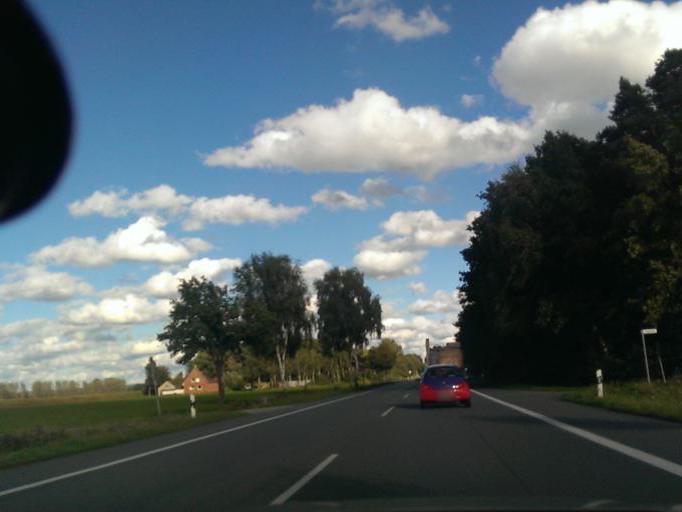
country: DE
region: North Rhine-Westphalia
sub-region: Regierungsbezirk Detmold
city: Delbruck
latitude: 51.7620
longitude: 8.6224
